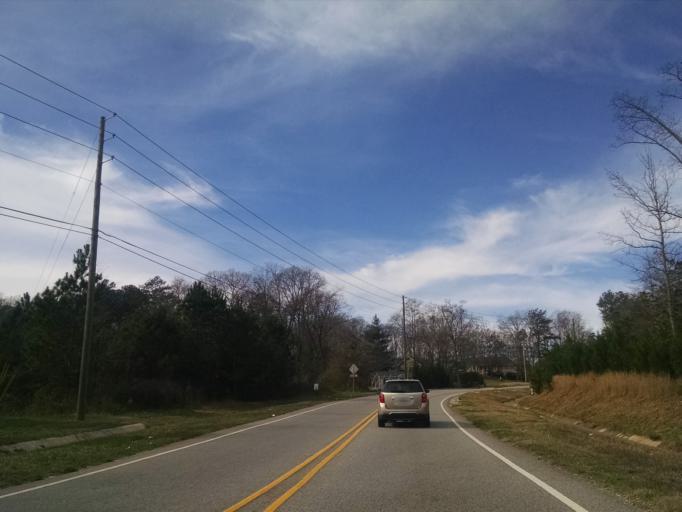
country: US
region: Georgia
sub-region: Gwinnett County
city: Sugar Hill
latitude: 34.0821
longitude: -84.0390
